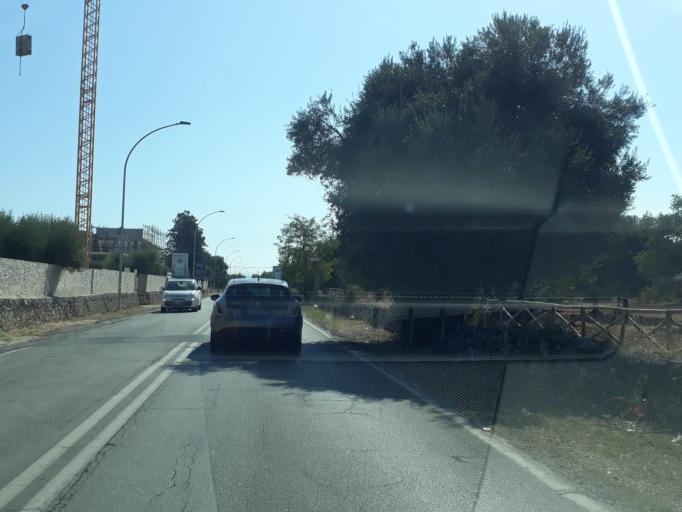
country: IT
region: Apulia
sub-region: Provincia di Bari
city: Monopoli
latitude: 40.9385
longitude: 17.3078
